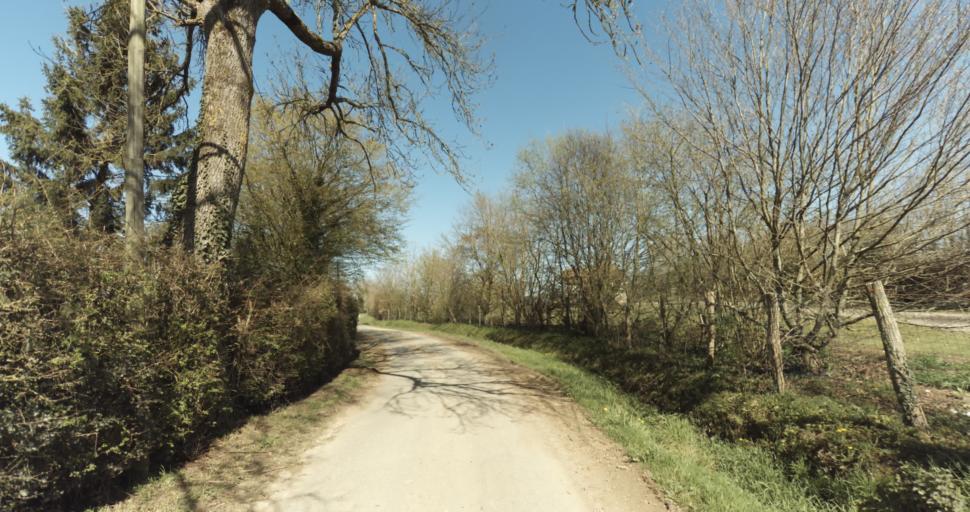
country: FR
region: Lower Normandy
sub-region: Departement du Calvados
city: Livarot
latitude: 49.0195
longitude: 0.1044
